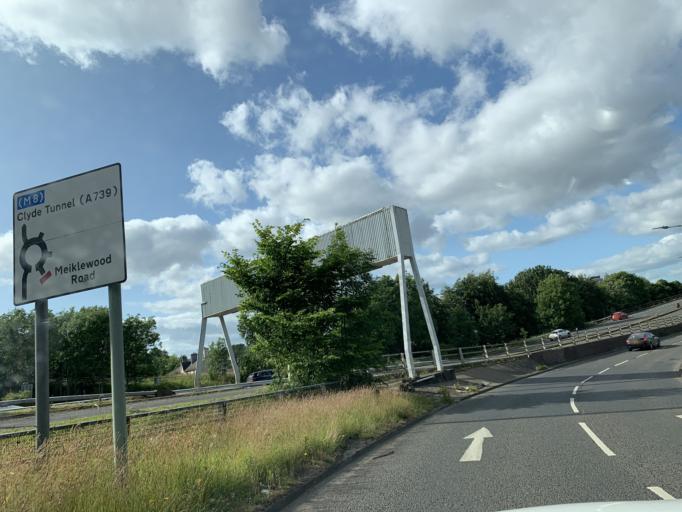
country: GB
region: Scotland
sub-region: Renfrewshire
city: Renfrew
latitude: 55.8549
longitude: -4.3412
